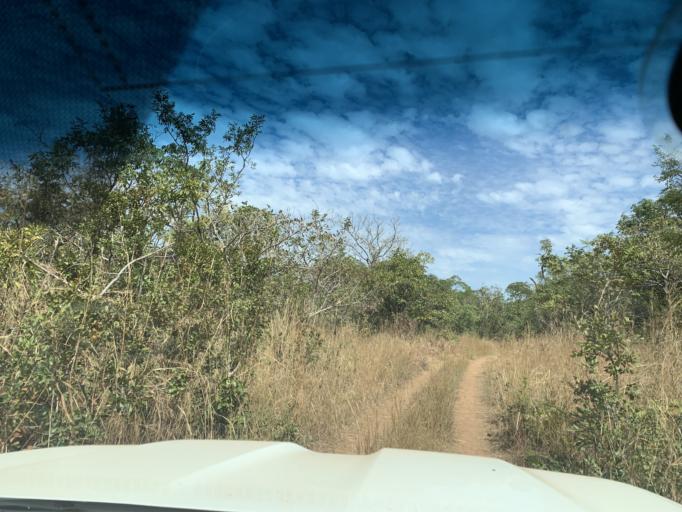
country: GN
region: Mamou
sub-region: Pita
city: Pita
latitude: 10.9911
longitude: -12.4895
